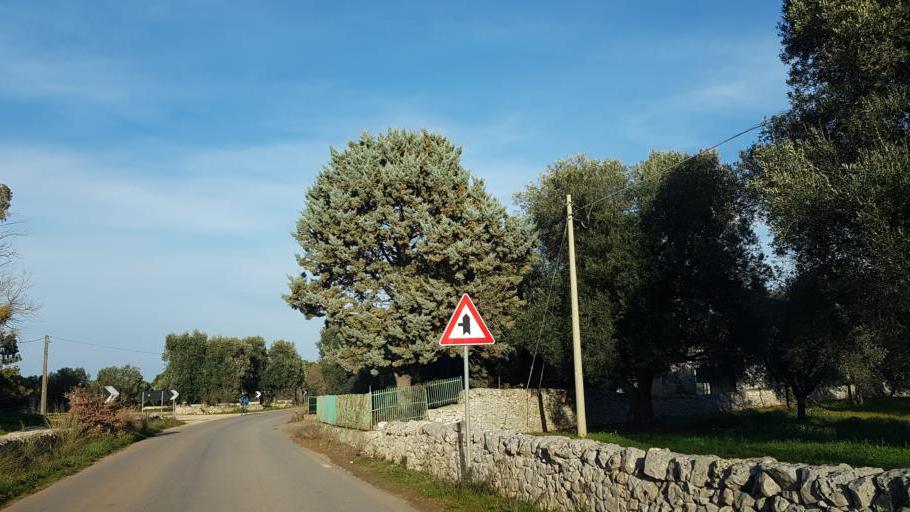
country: IT
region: Apulia
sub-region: Provincia di Brindisi
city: Carovigno
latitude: 40.7052
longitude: 17.6844
